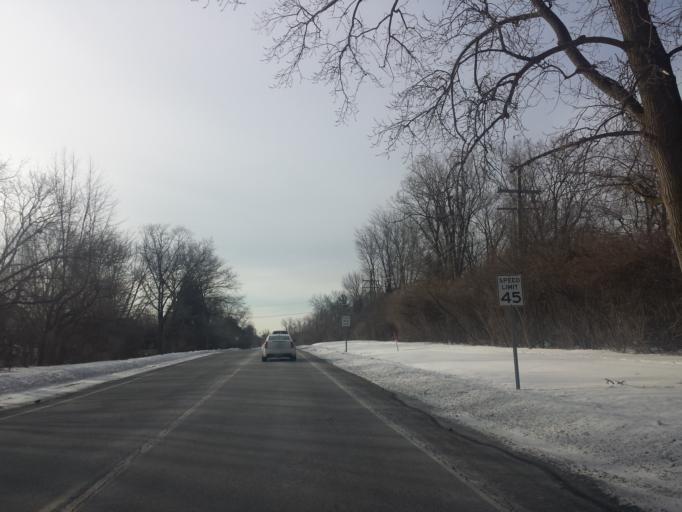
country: US
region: Michigan
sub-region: Oakland County
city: Franklin
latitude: 42.5354
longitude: -83.3408
